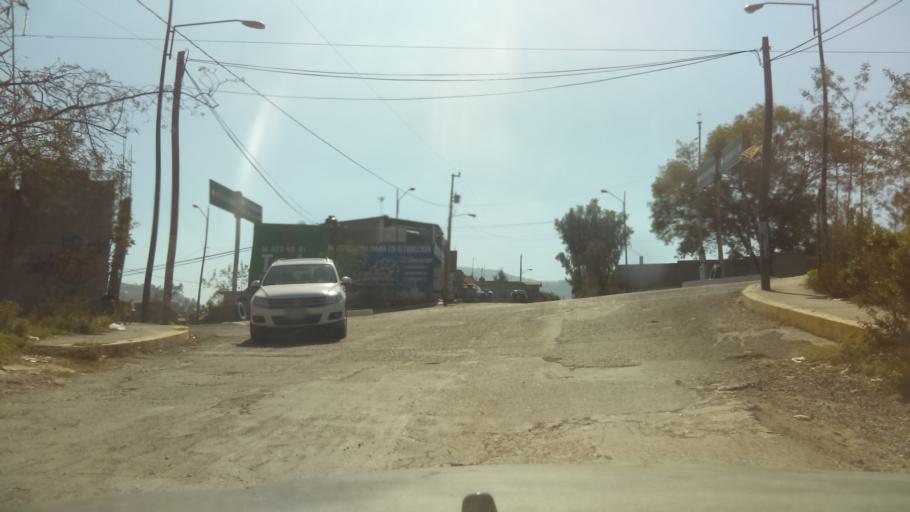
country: MX
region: Michoacan
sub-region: Morelia
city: Montana Monarca (Punta Altozano)
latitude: 19.6570
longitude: -101.1811
